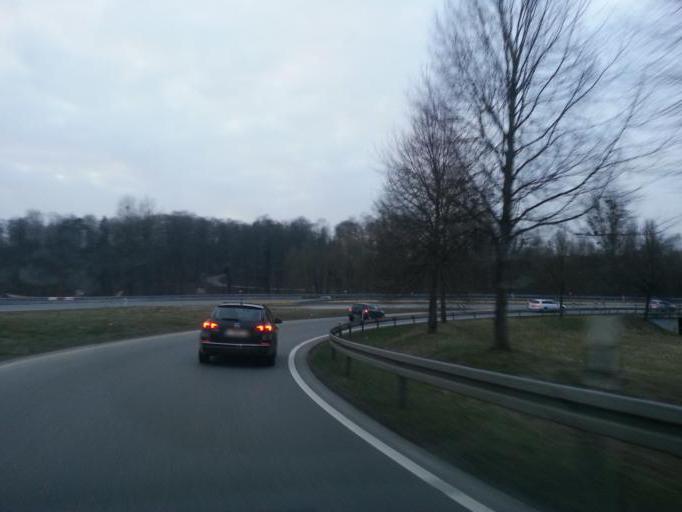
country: DE
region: Baden-Wuerttemberg
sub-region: Tuebingen Region
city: Ravensburg
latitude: 47.7666
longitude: 9.5902
